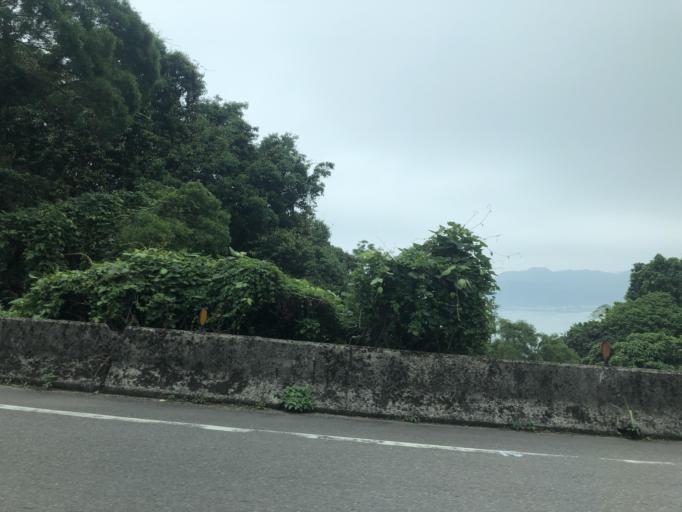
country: TW
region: Taiwan
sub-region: Keelung
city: Keelung
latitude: 25.1953
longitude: 121.6811
